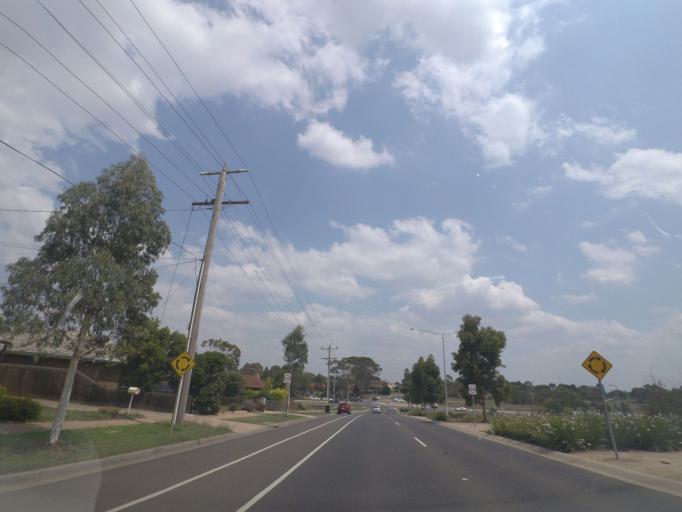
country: AU
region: Victoria
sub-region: Melton
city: Melton West
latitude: -37.6732
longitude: 144.5719
